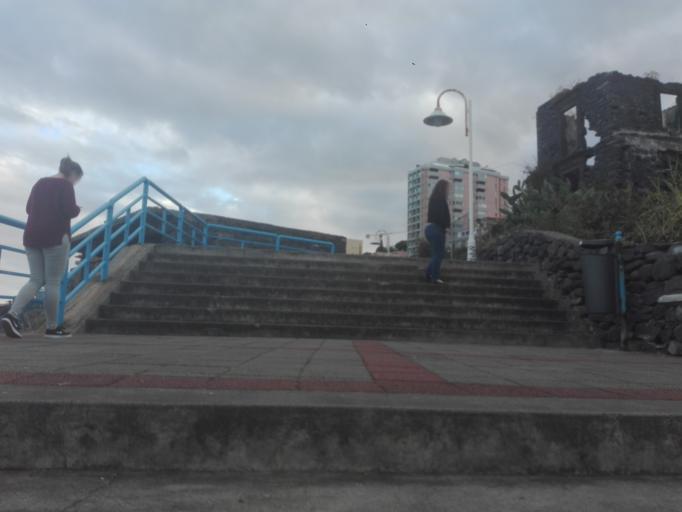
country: PT
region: Madeira
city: Canico
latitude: 32.6446
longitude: -16.8276
